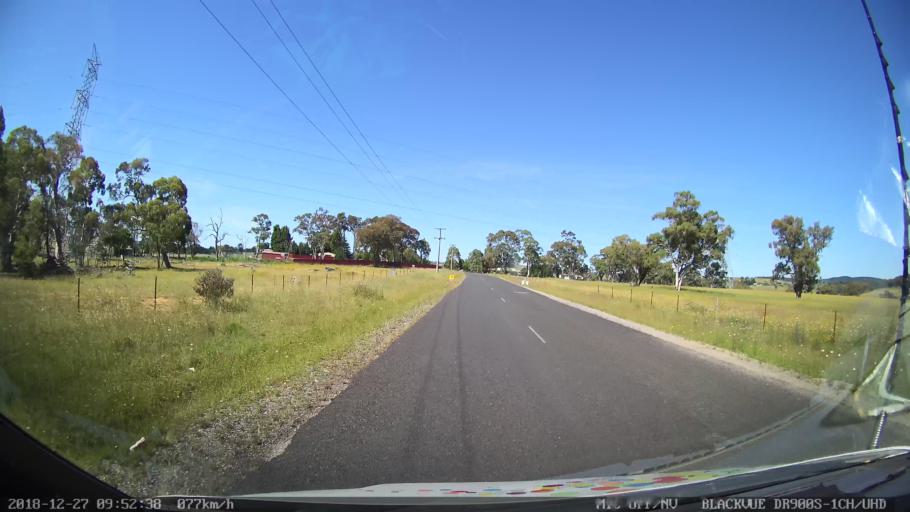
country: AU
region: New South Wales
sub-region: Lithgow
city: Portland
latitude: -33.3748
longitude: 149.9905
